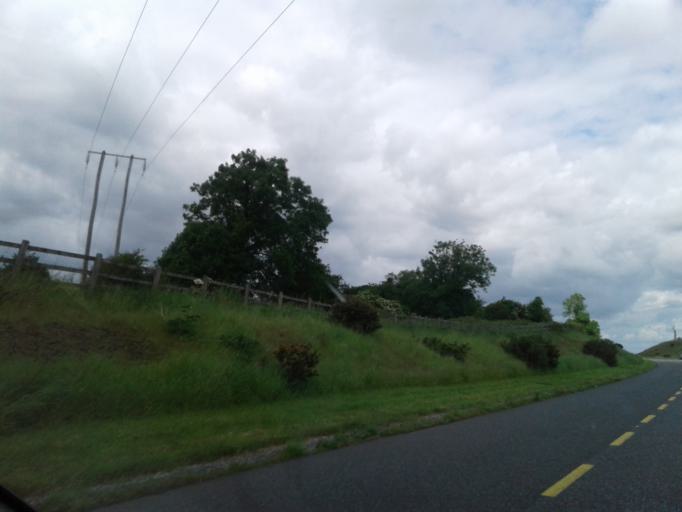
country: IE
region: Leinster
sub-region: Uibh Fhaili
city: Tullamore
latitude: 53.2973
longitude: -7.4831
